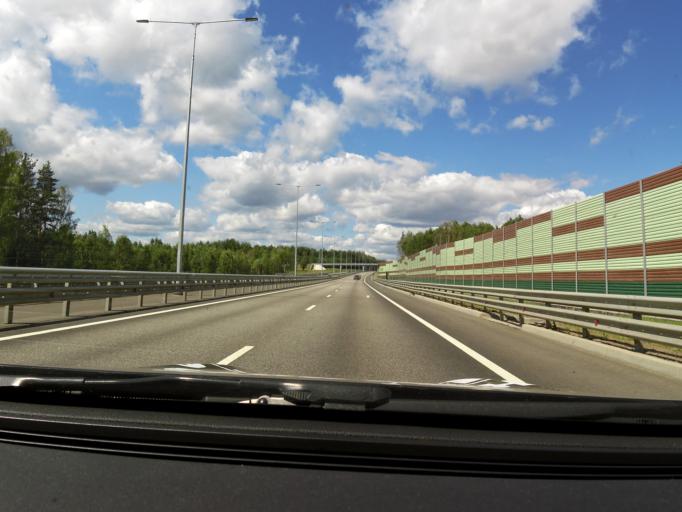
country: RU
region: Tverskaya
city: Vyshniy Volochek
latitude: 57.3748
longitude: 34.5982
